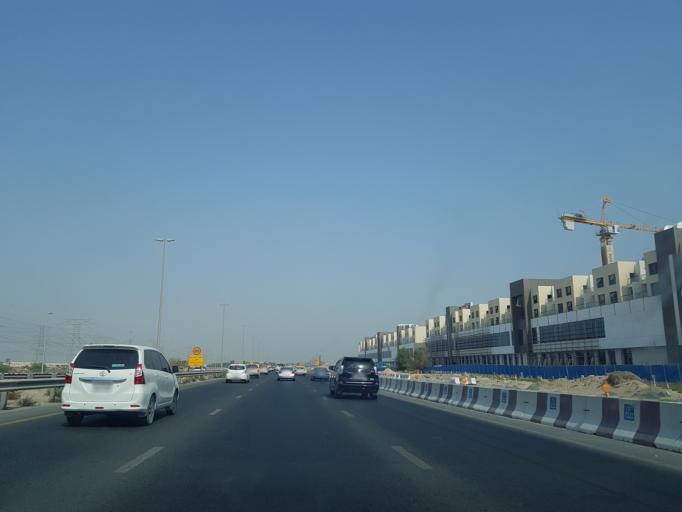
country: AE
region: Ash Shariqah
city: Sharjah
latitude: 25.1550
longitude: 55.4022
